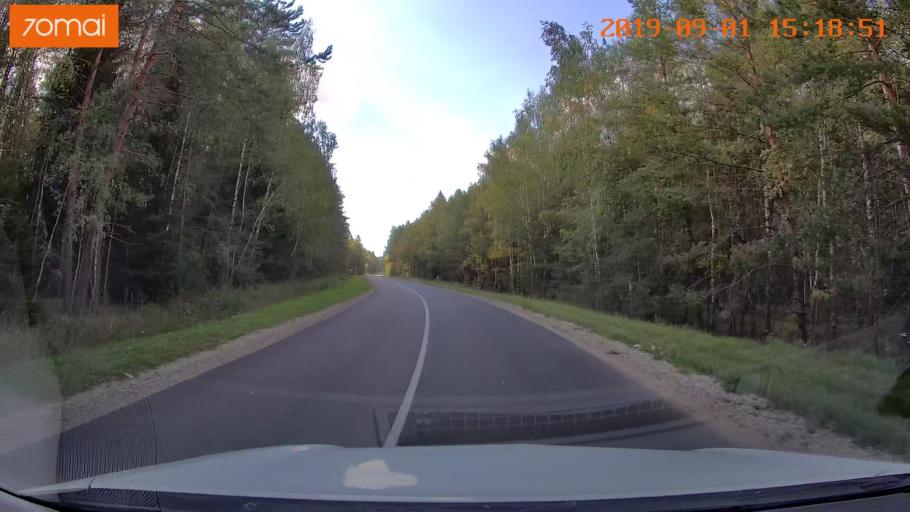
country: RU
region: Kaluga
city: Maloyaroslavets
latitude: 54.9107
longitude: 36.5039
